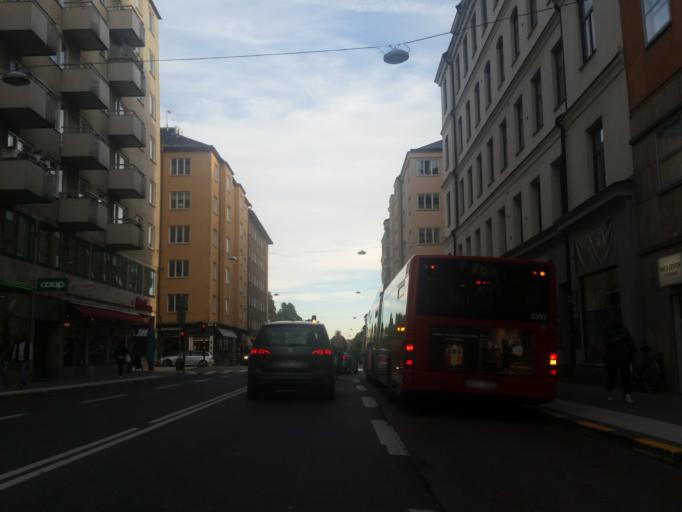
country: SE
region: Stockholm
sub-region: Stockholms Kommun
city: OEstermalm
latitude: 59.3141
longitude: 18.0845
